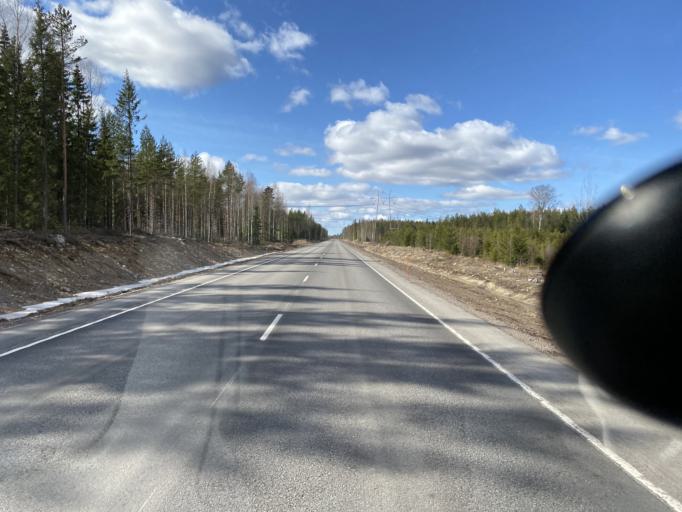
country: FI
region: Satakunta
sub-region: Pori
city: Huittinen
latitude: 61.1740
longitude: 22.5442
